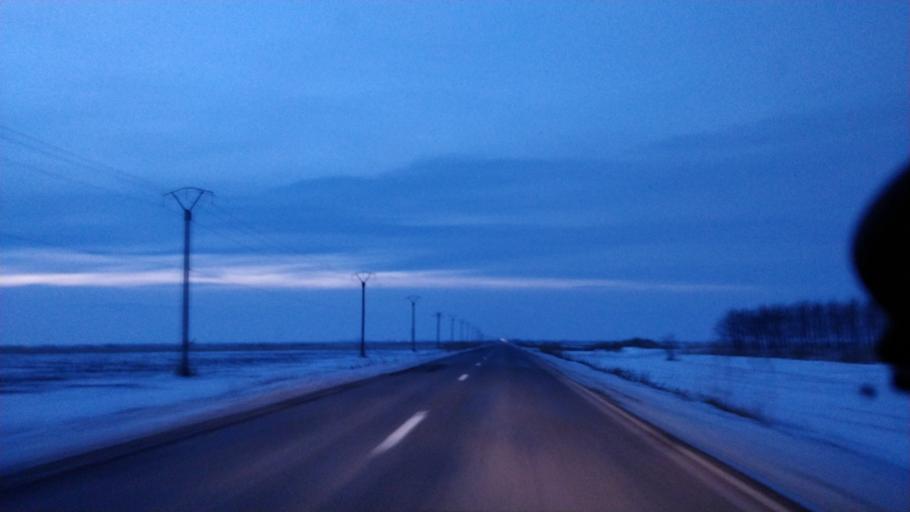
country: RO
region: Vrancea
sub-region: Comuna Vulturu
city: Vadu Rosca
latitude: 45.5968
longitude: 27.4662
